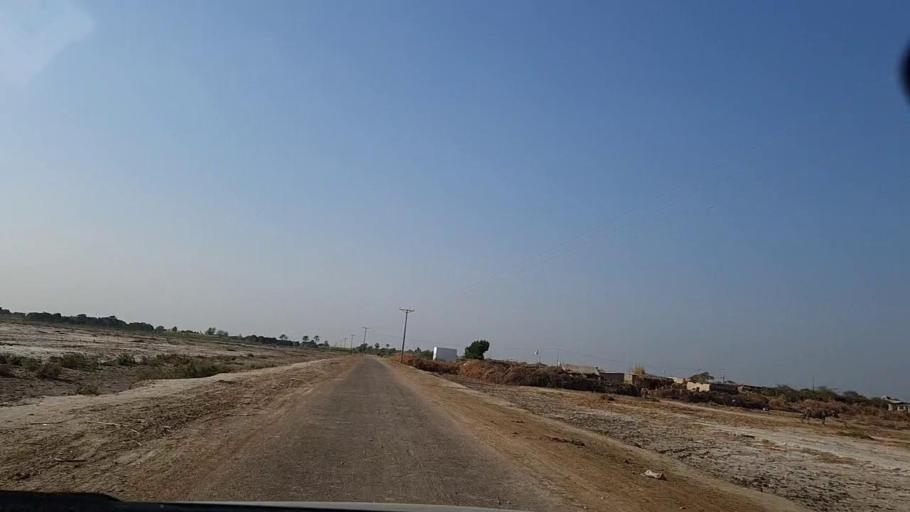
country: PK
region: Sindh
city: Mirwah Gorchani
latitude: 25.2163
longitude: 68.9939
